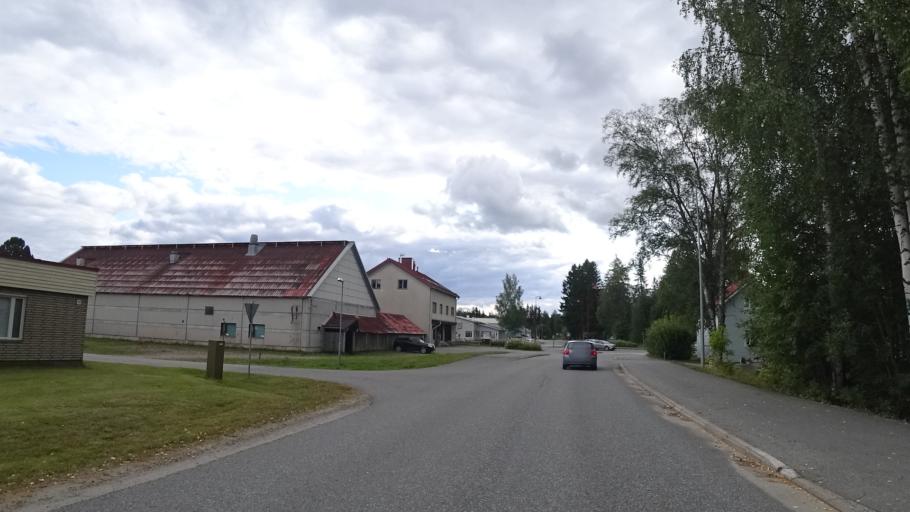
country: FI
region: North Karelia
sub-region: Joensuu
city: Ilomantsi
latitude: 62.6696
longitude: 30.9380
